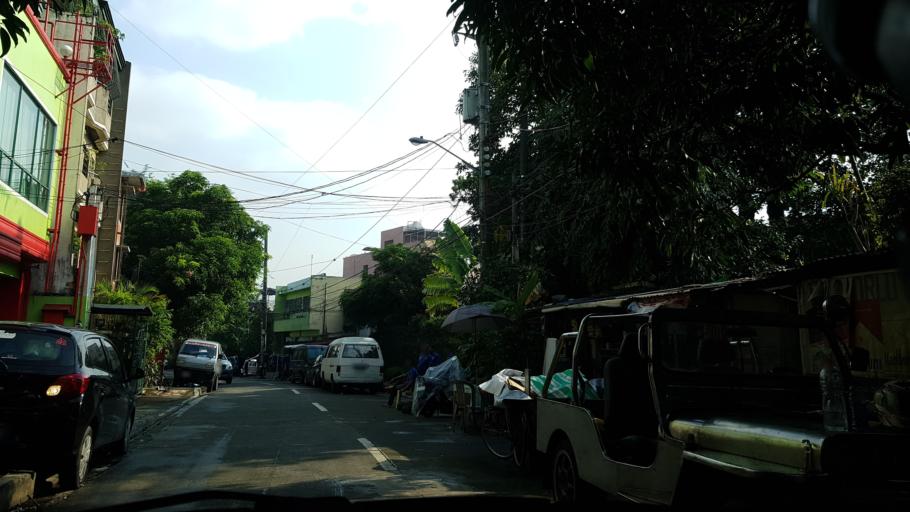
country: PH
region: Metro Manila
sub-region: Quezon City
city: Quezon City
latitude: 14.6336
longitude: 121.0478
